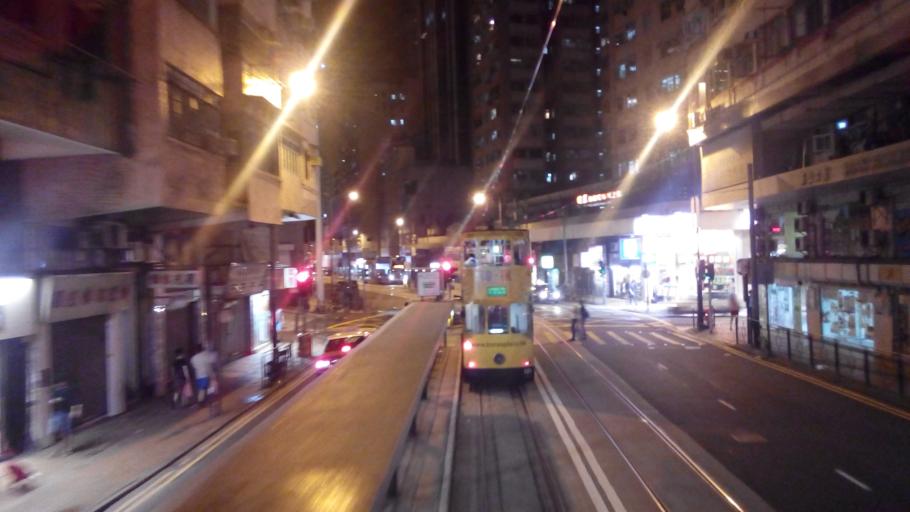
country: HK
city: Hong Kong
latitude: 22.2879
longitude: 114.1414
